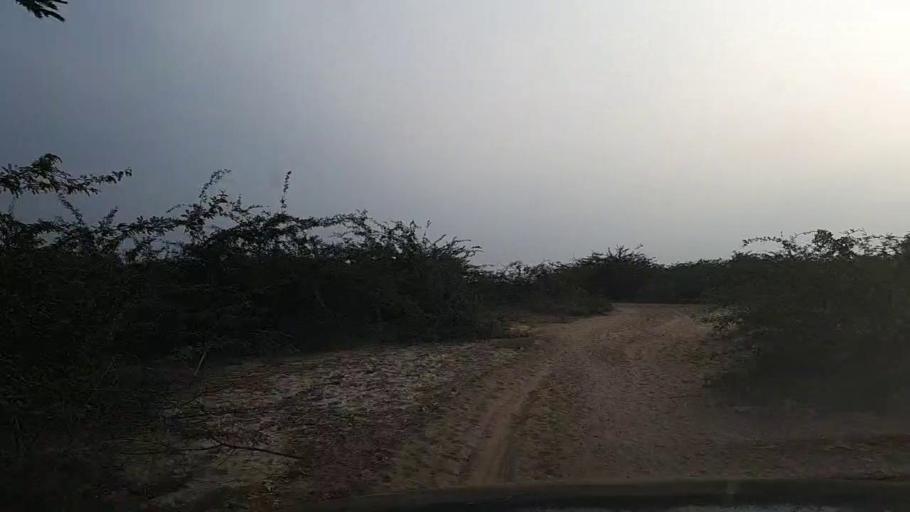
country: PK
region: Sindh
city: Gharo
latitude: 24.7823
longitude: 67.7153
